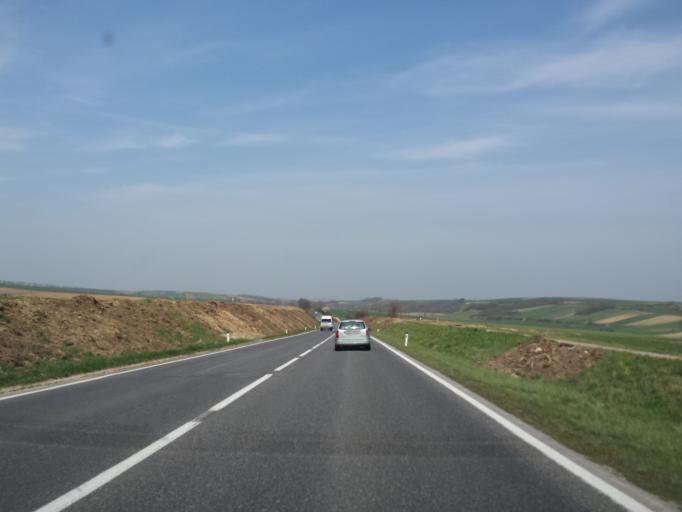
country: AT
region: Lower Austria
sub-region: Politischer Bezirk Mistelbach
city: Wilfersdorf
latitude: 48.6018
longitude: 16.6474
